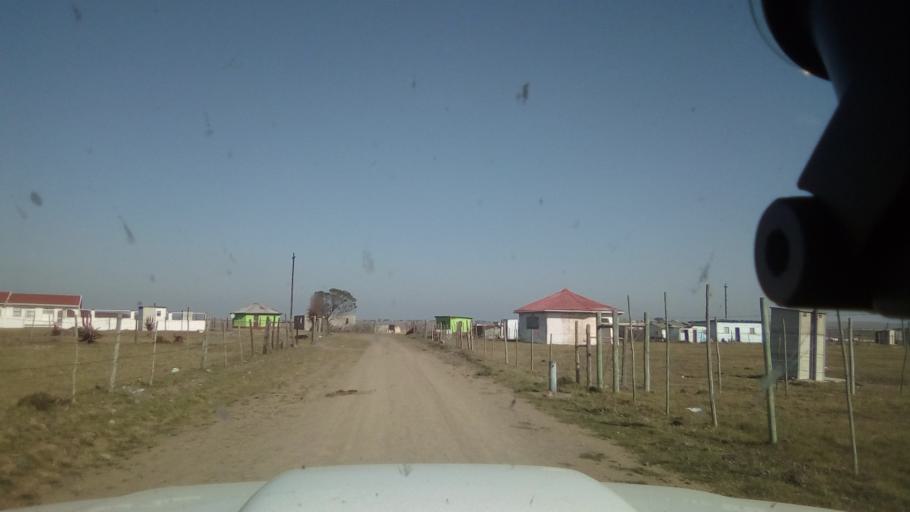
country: ZA
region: Eastern Cape
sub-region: Buffalo City Metropolitan Municipality
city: Bhisho
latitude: -32.9422
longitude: 27.3348
